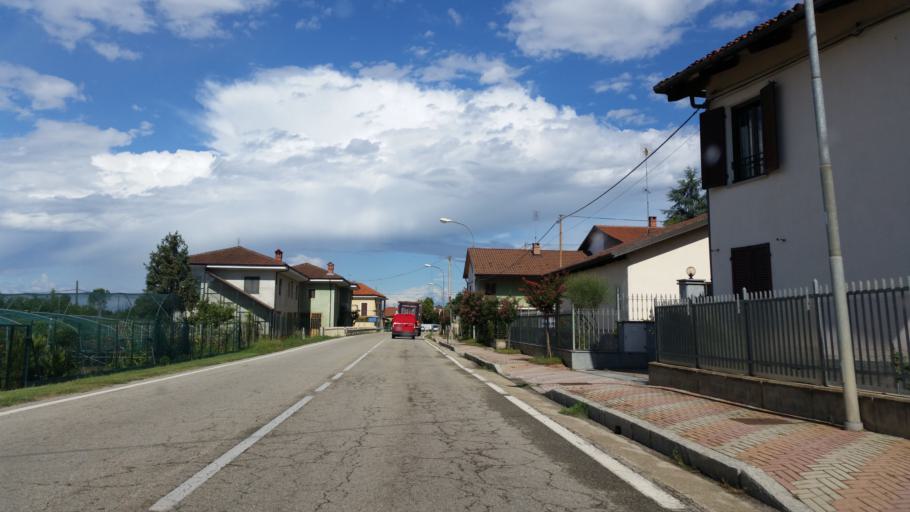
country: IT
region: Piedmont
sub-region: Provincia di Torino
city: Pralormo
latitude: 44.8584
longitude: 7.9021
